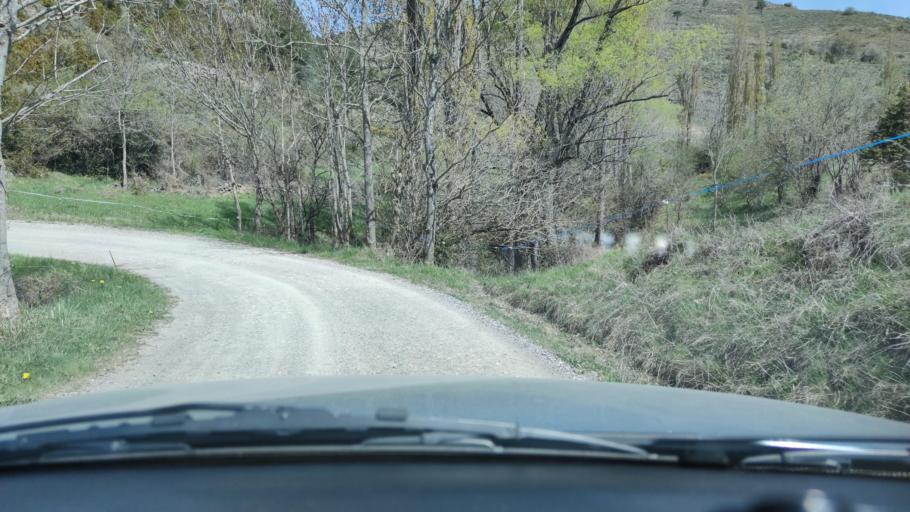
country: ES
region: Catalonia
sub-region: Provincia de Lleida
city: Sort
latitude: 42.2934
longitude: 1.1878
